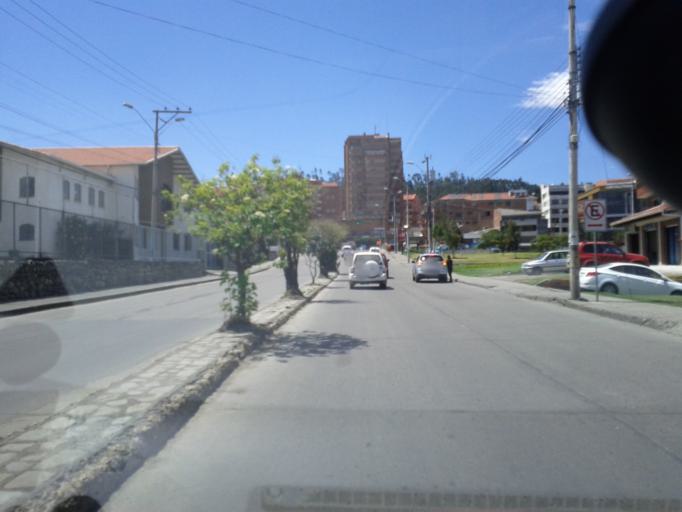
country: EC
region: Azuay
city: Cuenca
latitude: -2.8941
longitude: -79.0189
